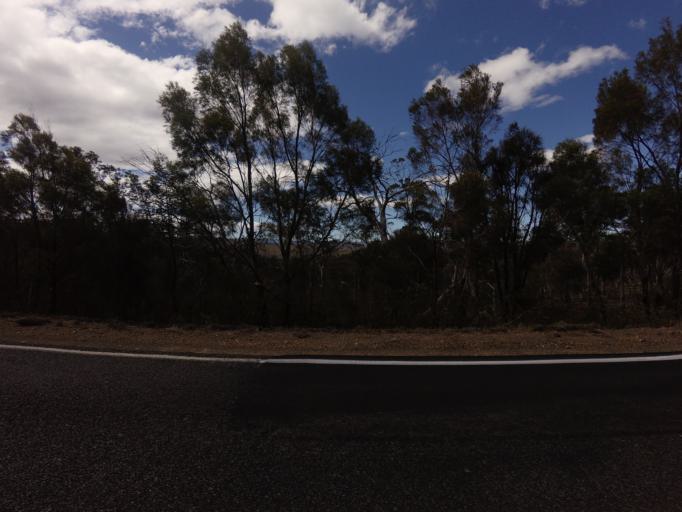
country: AU
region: Tasmania
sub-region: Break O'Day
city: St Helens
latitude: -42.0156
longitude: 147.9817
